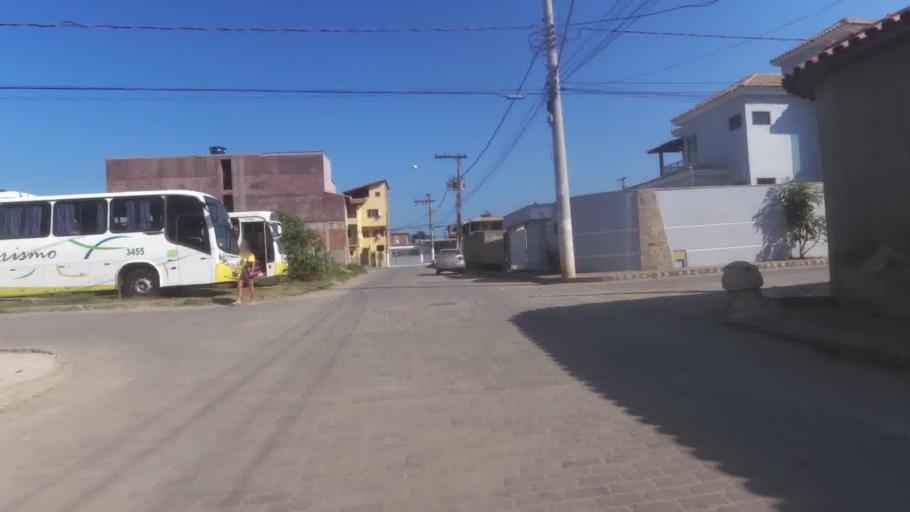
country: BR
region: Espirito Santo
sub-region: Itapemirim
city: Itapemirim
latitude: -21.0197
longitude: -40.8165
